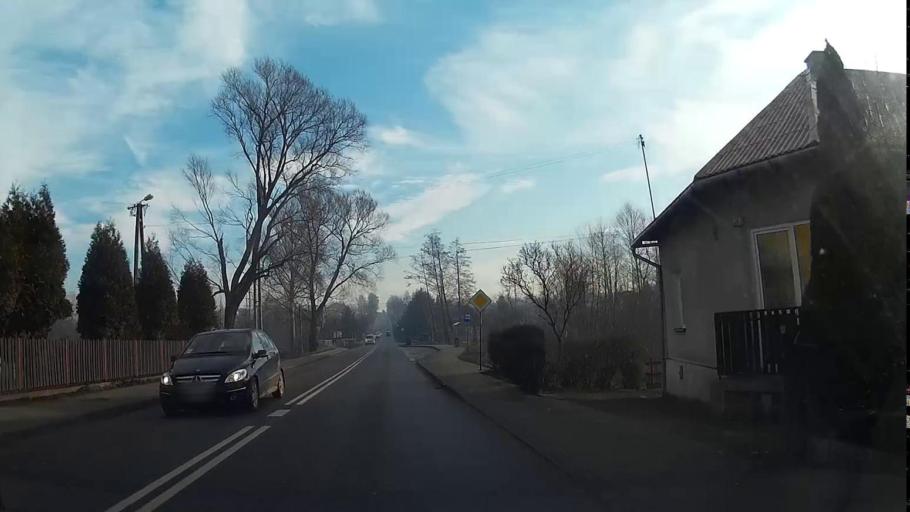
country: PL
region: Lesser Poland Voivodeship
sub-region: Powiat chrzanowski
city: Alwernia
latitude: 50.0587
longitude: 19.5269
